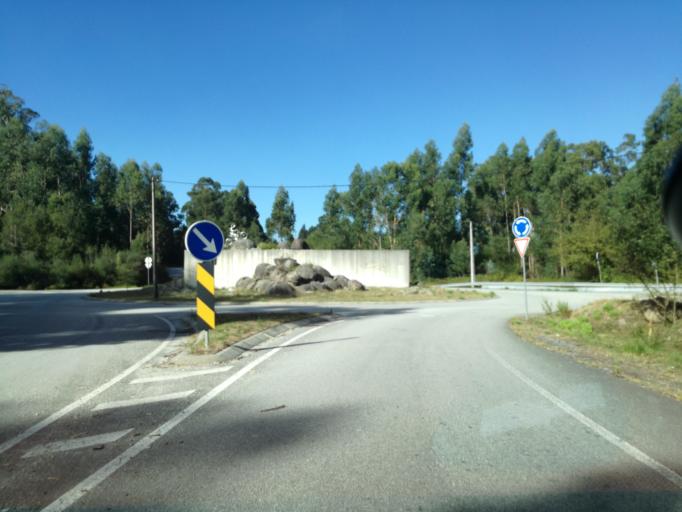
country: PT
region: Porto
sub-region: Pacos de Ferreira
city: Seroa
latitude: 41.2894
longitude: -8.4225
